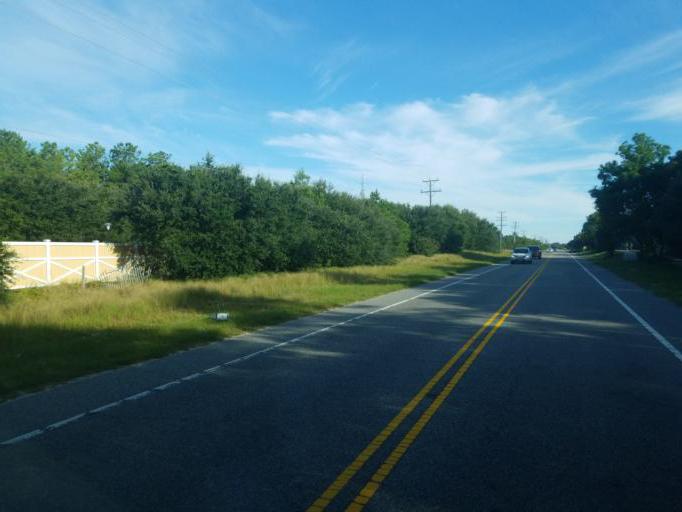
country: US
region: North Carolina
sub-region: Dare County
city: Southern Shores
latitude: 36.3176
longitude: -75.8142
